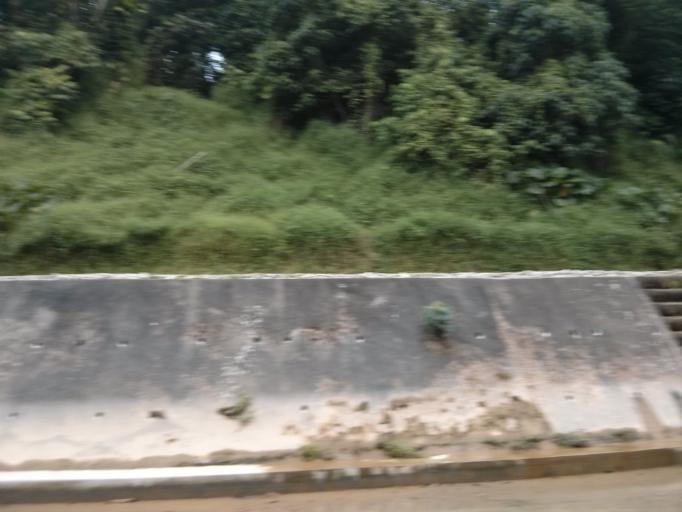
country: SG
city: Singapore
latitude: 1.3252
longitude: 103.7802
